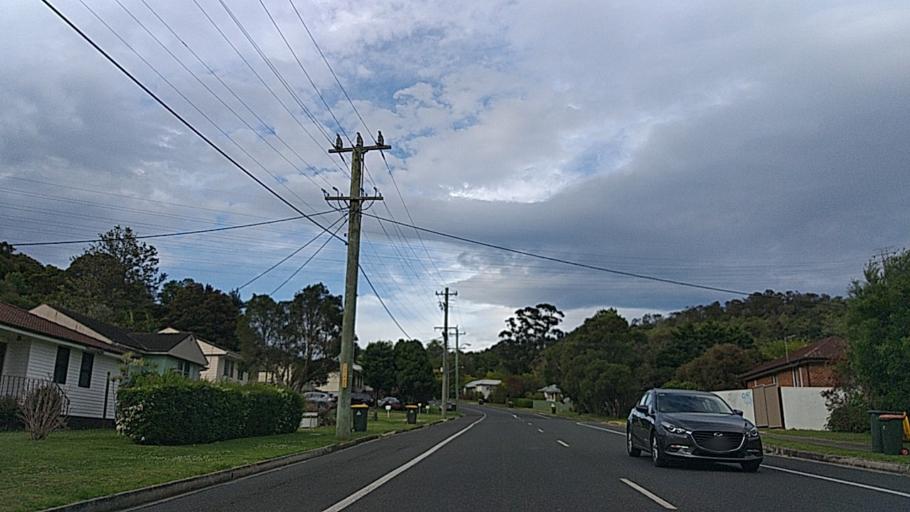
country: AU
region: New South Wales
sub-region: Wollongong
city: Berkeley
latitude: -34.4727
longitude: 150.8431
